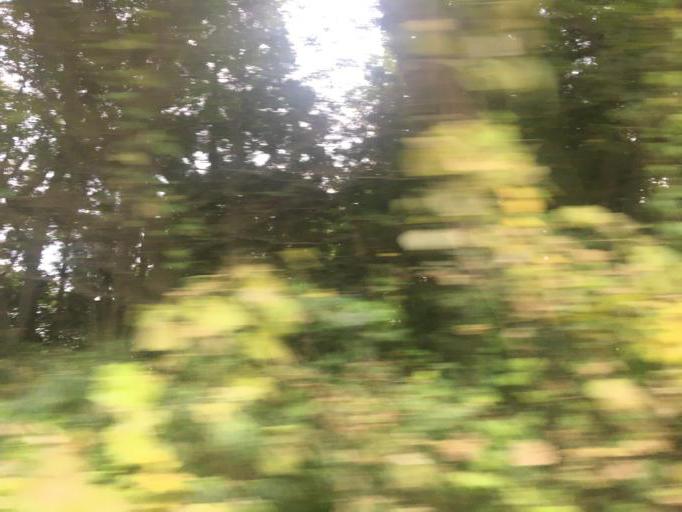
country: JP
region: Tokyo
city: Hino
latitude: 35.6792
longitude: 139.3695
